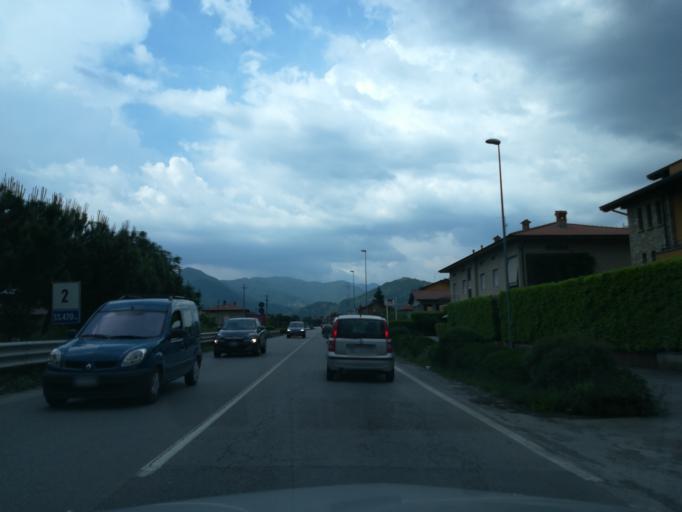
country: IT
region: Lombardy
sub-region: Provincia di Bergamo
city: Paladina
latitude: 45.7297
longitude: 9.6091
